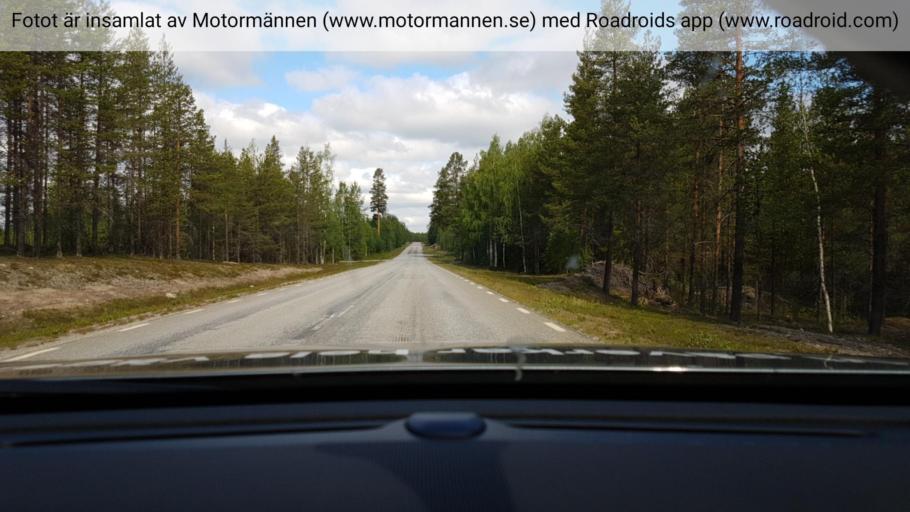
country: SE
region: Vaesterbotten
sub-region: Lycksele Kommun
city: Lycksele
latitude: 64.8343
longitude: 18.7779
